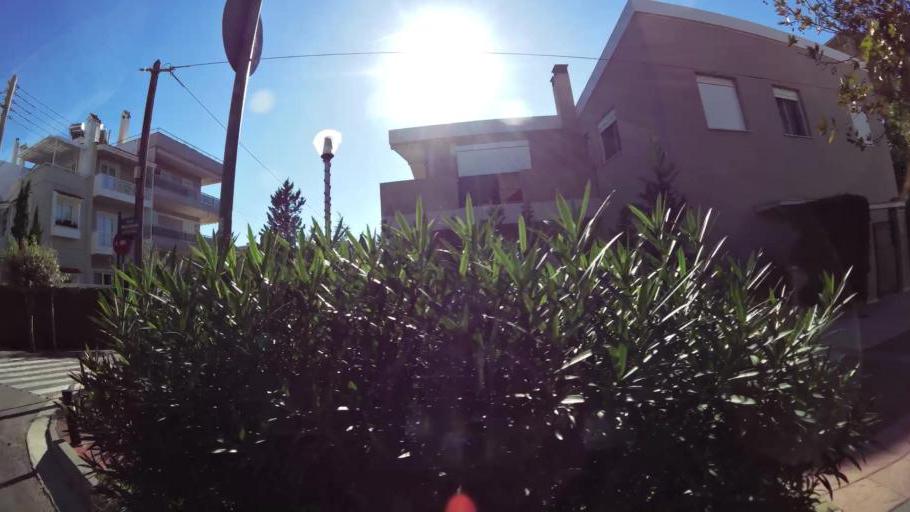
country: GR
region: Attica
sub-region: Nomarchia Athinas
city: Vrilissia
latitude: 38.0396
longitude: 23.8347
